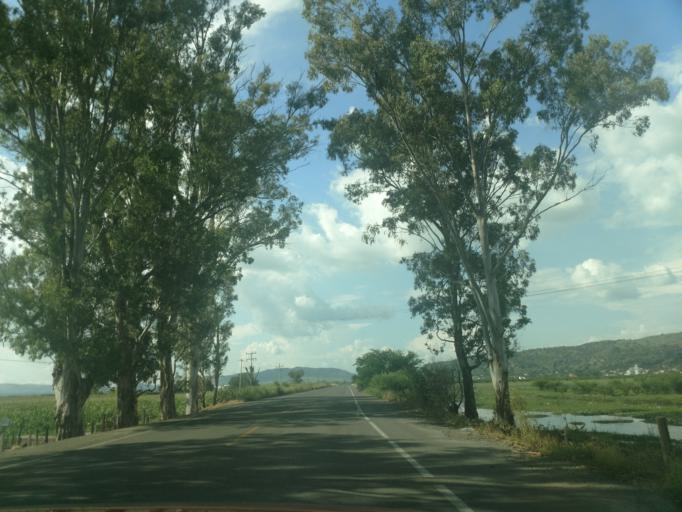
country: MX
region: Jalisco
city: Antonio Escobedo
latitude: 20.8939
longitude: -103.9936
